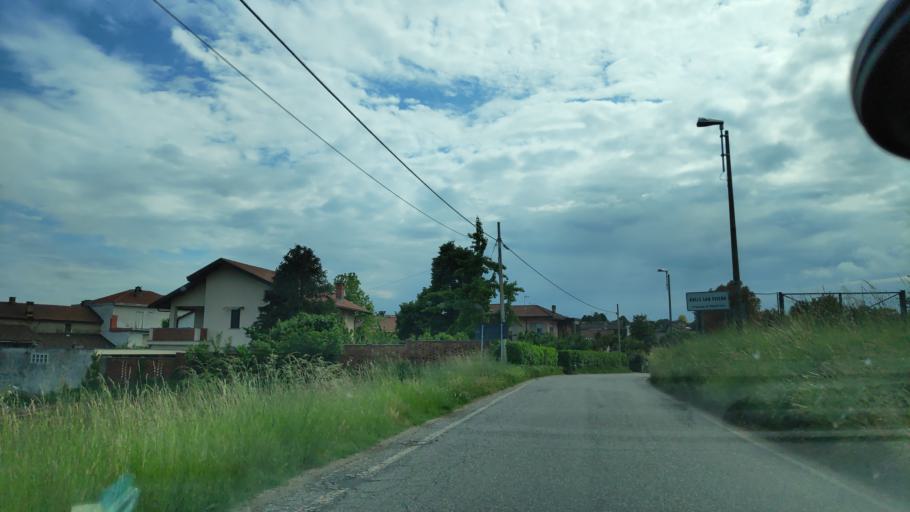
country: IT
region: Piedmont
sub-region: Provincia di Torino
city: Pecetto
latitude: 45.0098
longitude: 7.7633
